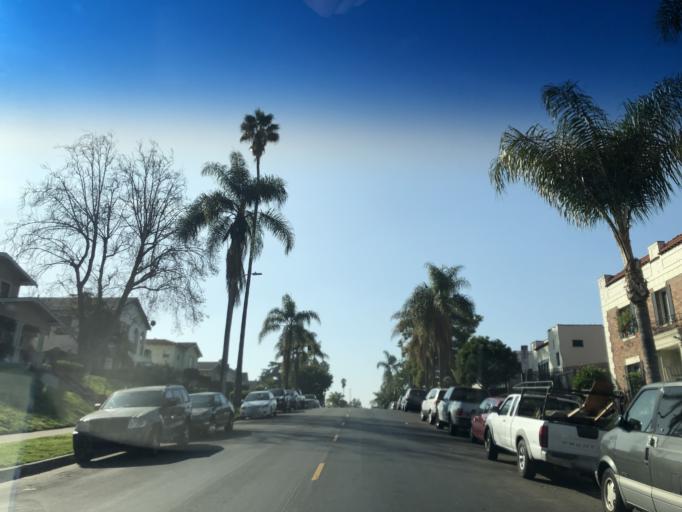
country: US
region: California
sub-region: Los Angeles County
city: Hollywood
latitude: 34.0512
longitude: -118.3221
